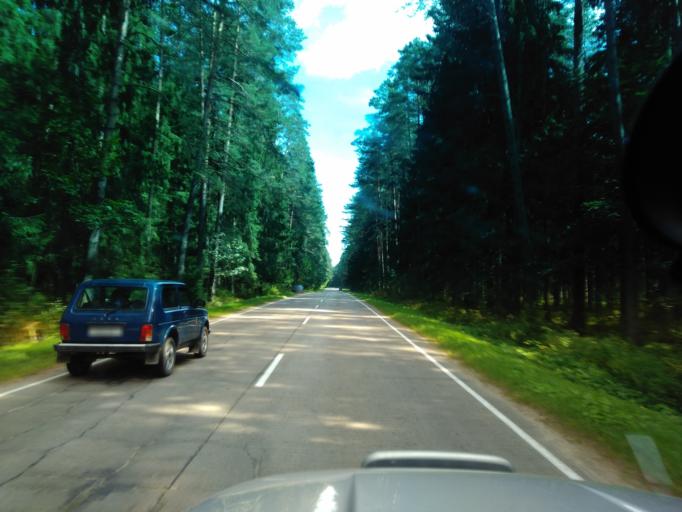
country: BY
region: Minsk
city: Stan'kava
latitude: 53.6221
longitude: 27.3014
